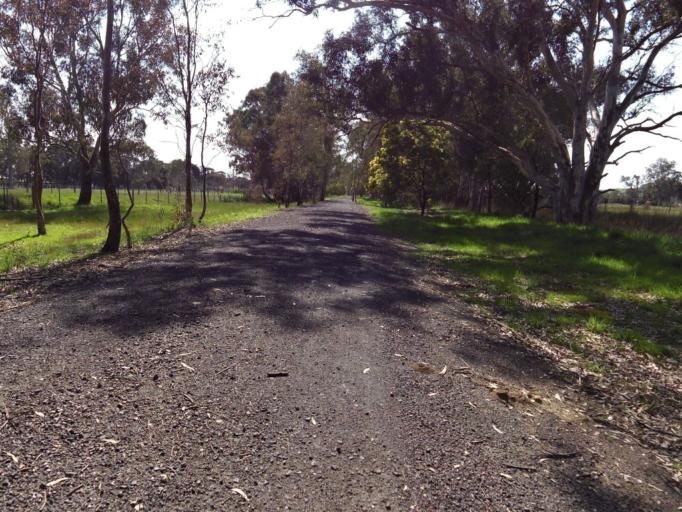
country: AU
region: Victoria
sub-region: Murrindindi
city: Alexandra
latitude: -37.1087
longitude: 145.6134
